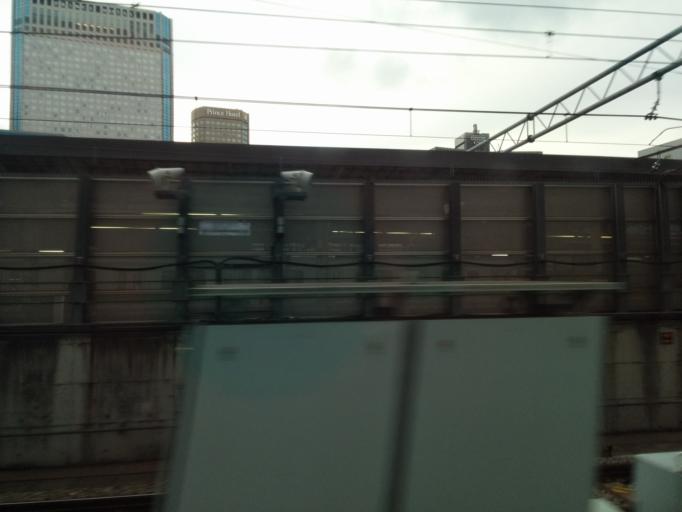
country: JP
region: Tokyo
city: Tokyo
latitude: 35.6278
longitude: 139.7398
